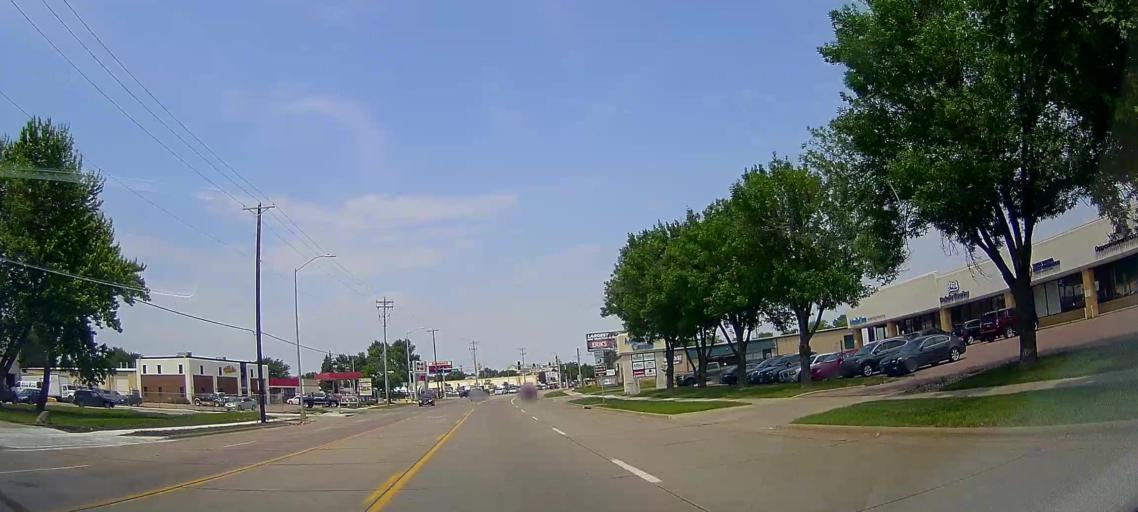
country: US
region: South Dakota
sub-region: Minnehaha County
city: Sioux Falls
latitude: 43.5073
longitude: -96.7506
